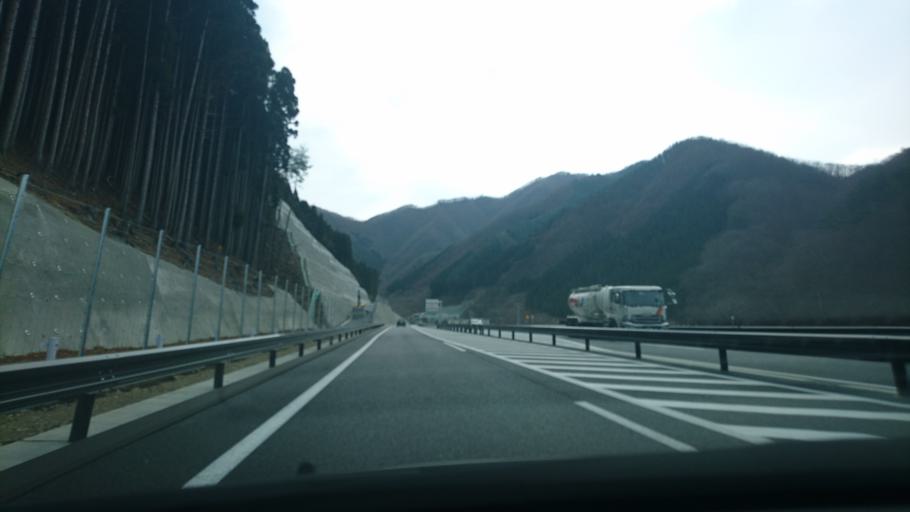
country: JP
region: Iwate
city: Kamaishi
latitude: 39.2458
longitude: 141.8421
